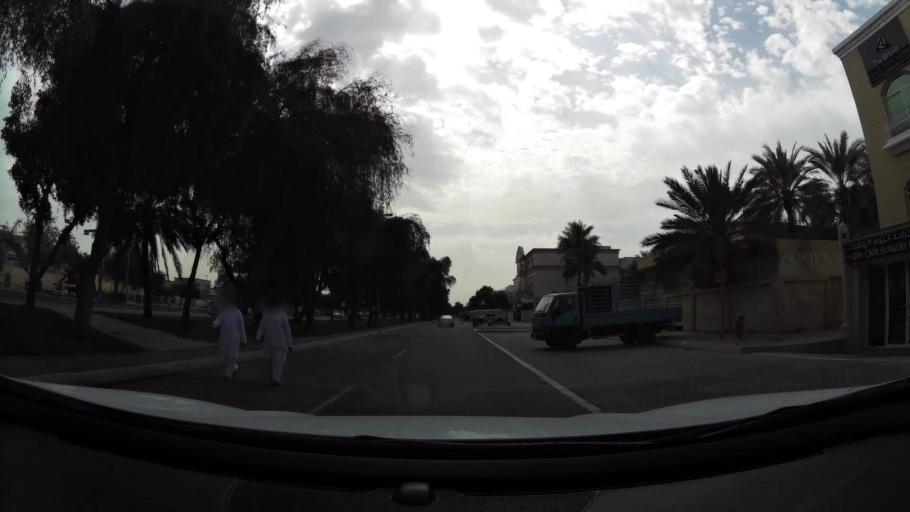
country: AE
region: Abu Dhabi
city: Abu Dhabi
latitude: 24.4426
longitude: 54.3683
